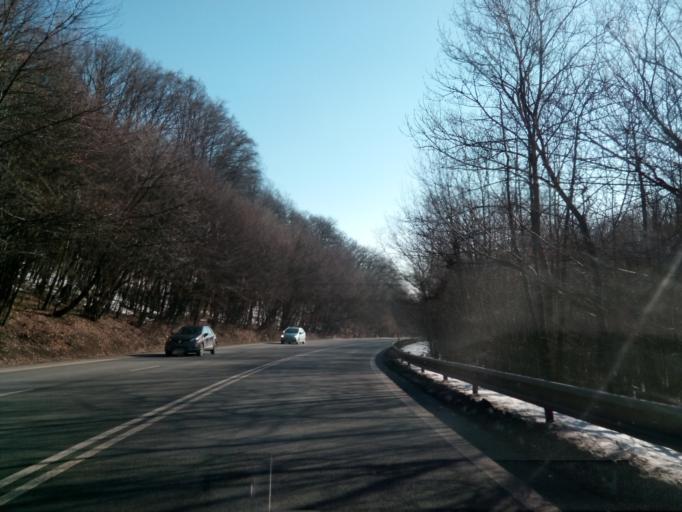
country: SK
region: Kosicky
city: Secovce
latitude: 48.7352
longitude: 21.5587
